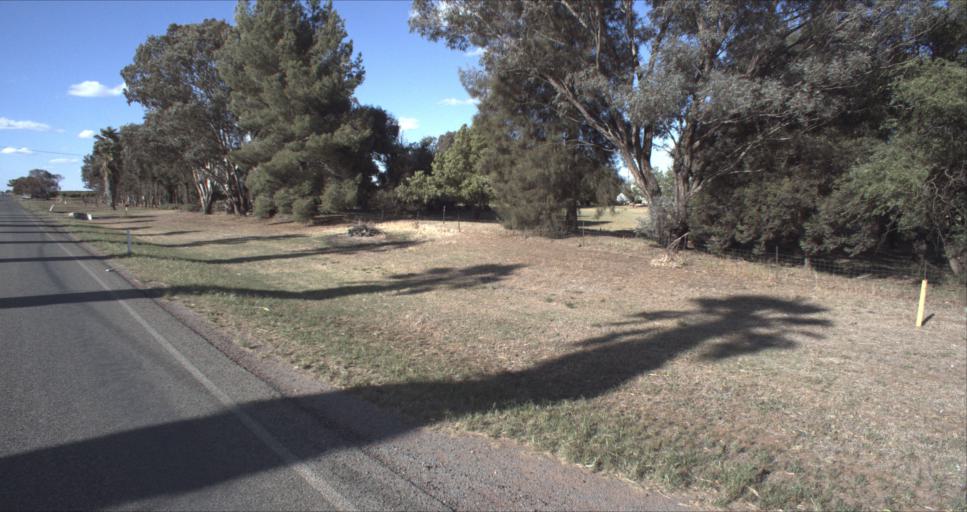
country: AU
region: New South Wales
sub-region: Leeton
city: Leeton
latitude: -34.5252
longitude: 146.2825
